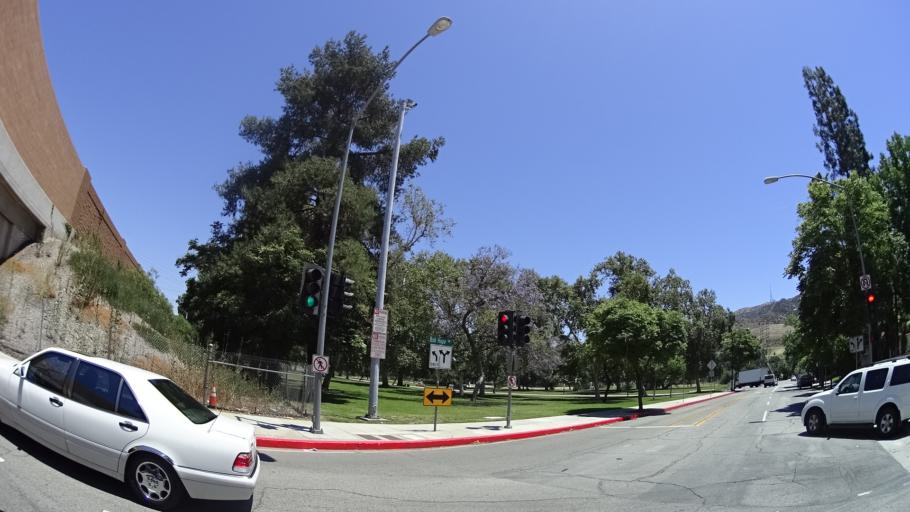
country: US
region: California
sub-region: Los Angeles County
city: Universal City
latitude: 34.1526
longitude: -118.3302
